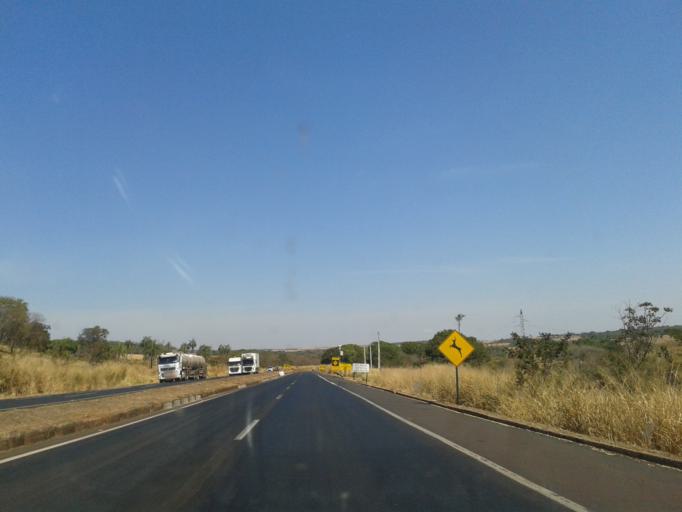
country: BR
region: Minas Gerais
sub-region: Monte Alegre De Minas
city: Monte Alegre de Minas
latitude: -18.7834
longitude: -49.0813
